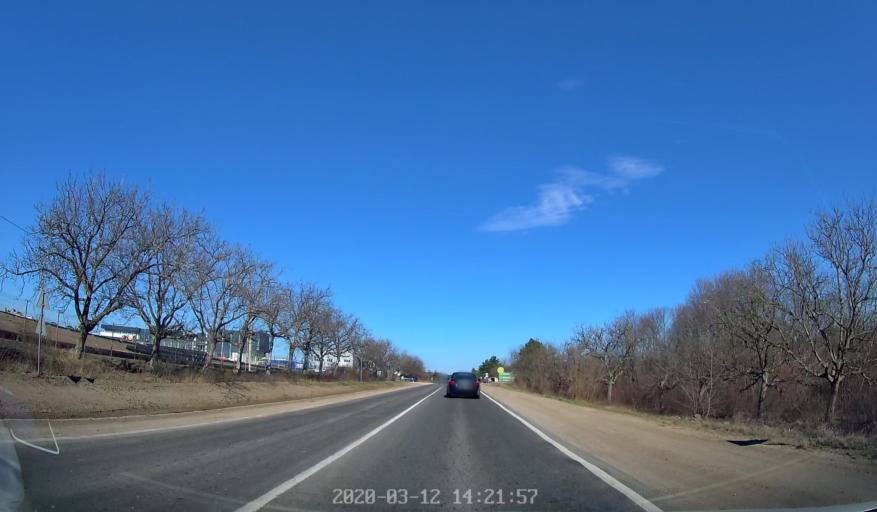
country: MD
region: Chisinau
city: Vatra
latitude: 47.0655
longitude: 28.7980
